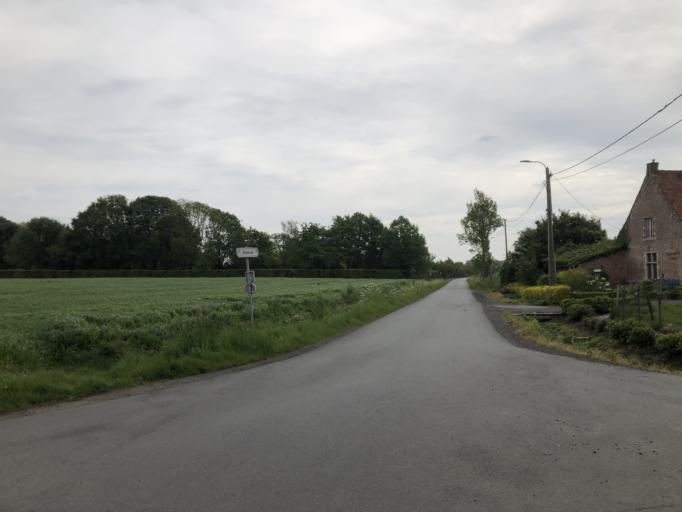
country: BE
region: Flanders
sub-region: Provincie Oost-Vlaanderen
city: Kruibeke
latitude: 51.2000
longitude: 4.2977
